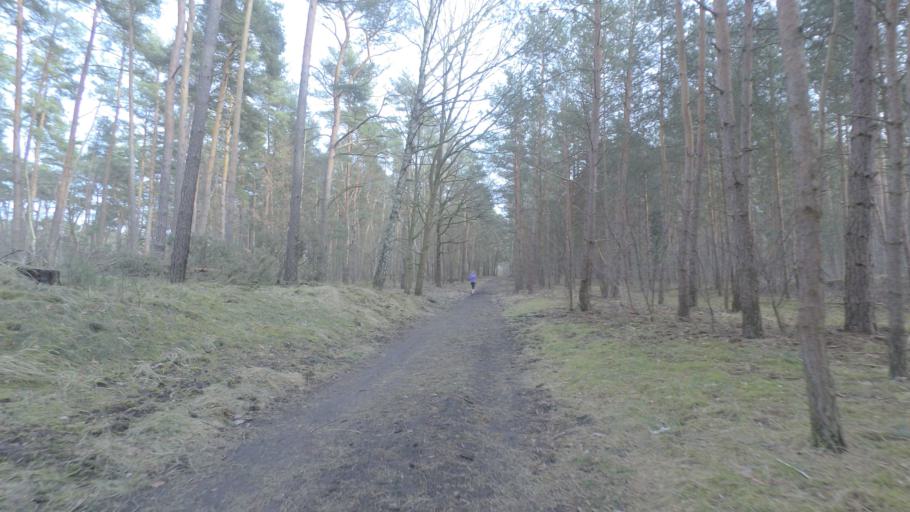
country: DE
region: Brandenburg
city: Ludwigsfelde
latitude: 52.2999
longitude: 13.2414
